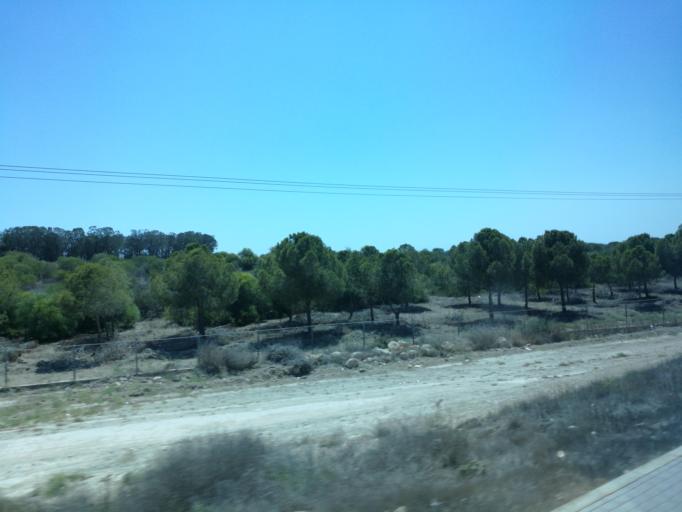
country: CY
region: Ammochostos
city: Famagusta
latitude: 35.1759
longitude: 33.8973
